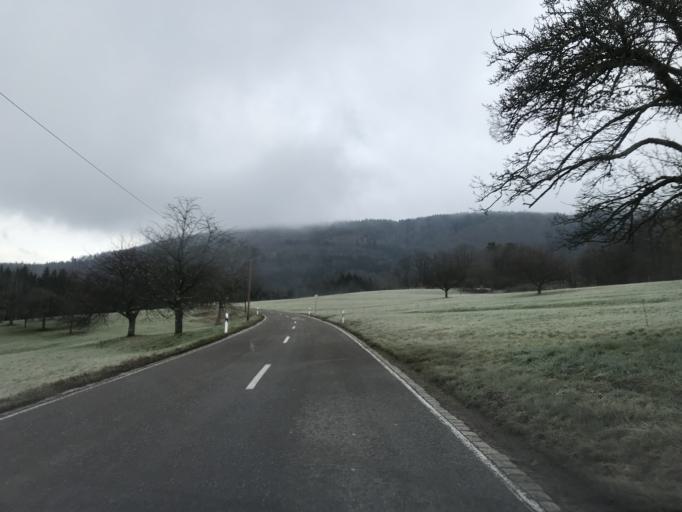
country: DE
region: Baden-Wuerttemberg
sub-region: Freiburg Region
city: Wehr
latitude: 47.6212
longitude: 7.9146
